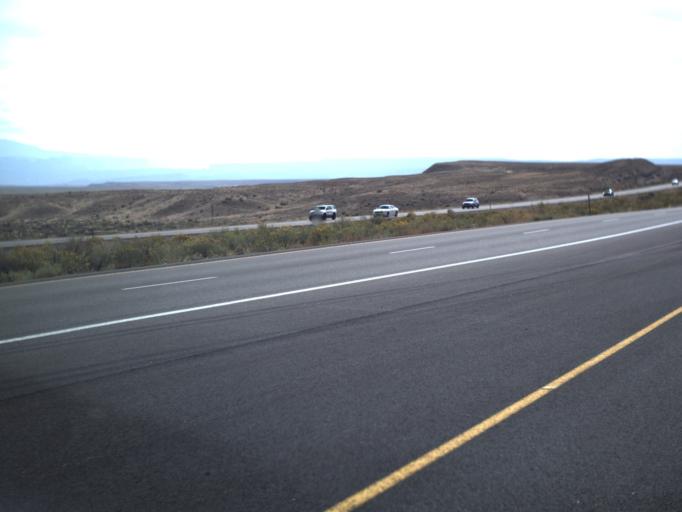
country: US
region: Colorado
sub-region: Mesa County
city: Loma
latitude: 39.0342
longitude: -109.2872
